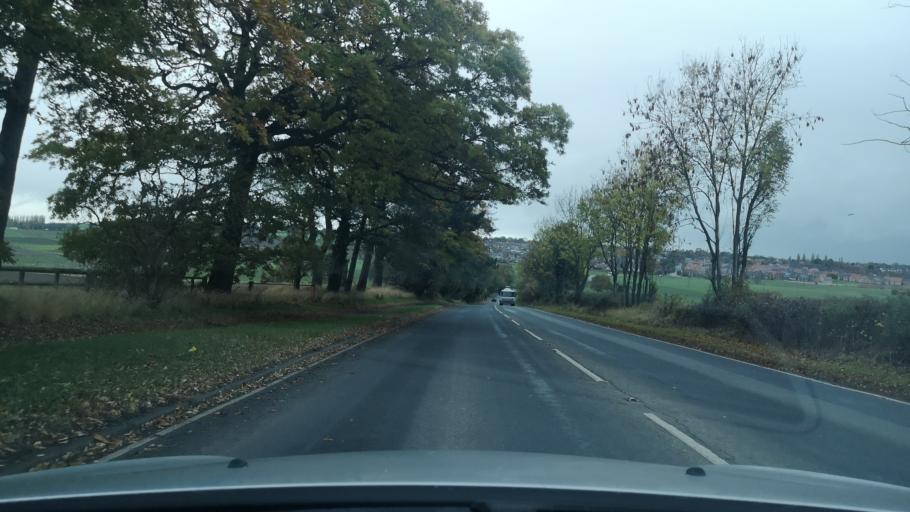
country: GB
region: England
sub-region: City and Borough of Wakefield
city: Low Ackworth
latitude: 53.6680
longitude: -1.3246
